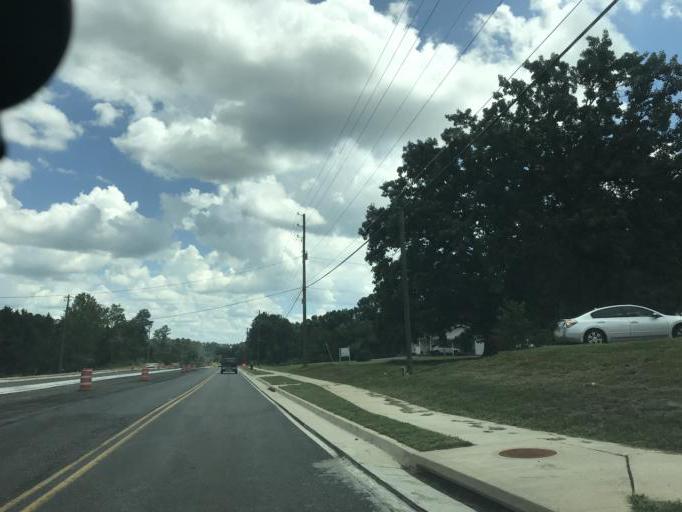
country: US
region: Georgia
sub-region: Forsyth County
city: Cumming
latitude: 34.2320
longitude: -84.1944
